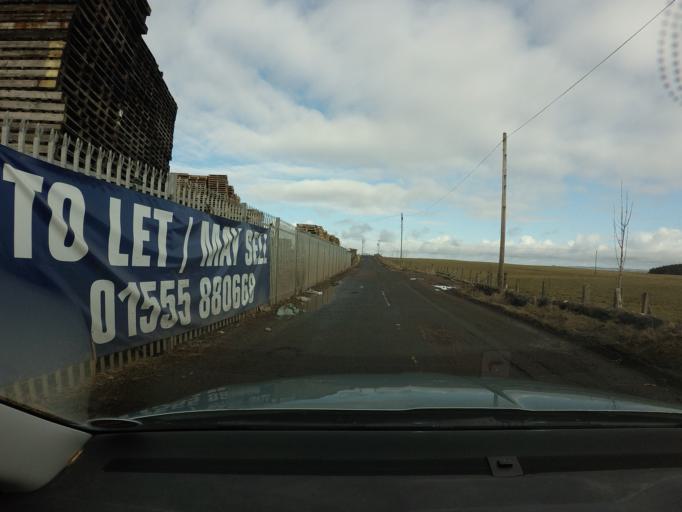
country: GB
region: Scotland
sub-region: South Lanarkshire
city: Lanark
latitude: 55.5998
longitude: -3.7719
